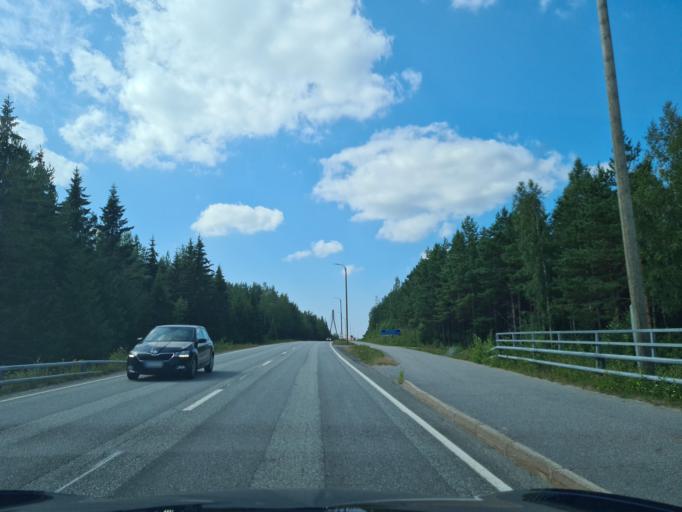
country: FI
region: Ostrobothnia
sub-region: Vaasa
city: Replot
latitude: 63.2055
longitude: 21.4995
